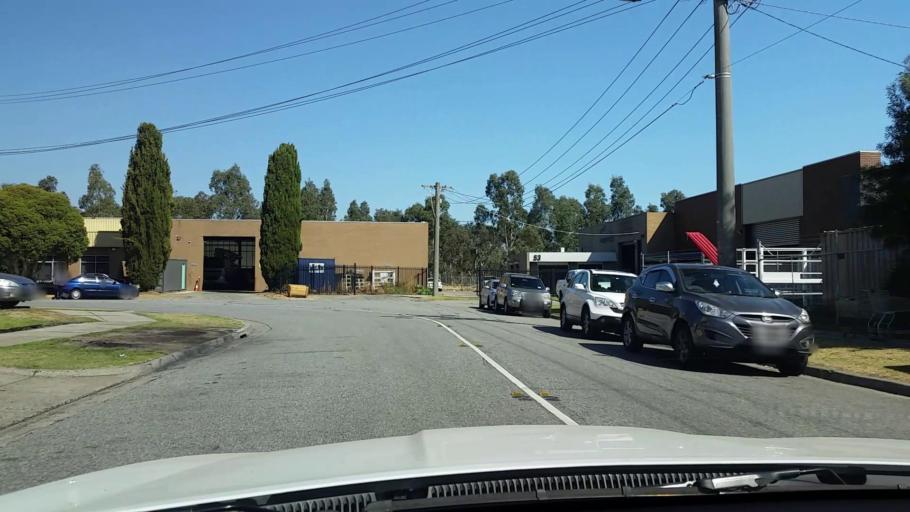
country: AU
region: Victoria
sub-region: Greater Dandenong
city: Dandenong
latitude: -38.0023
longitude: 145.2136
